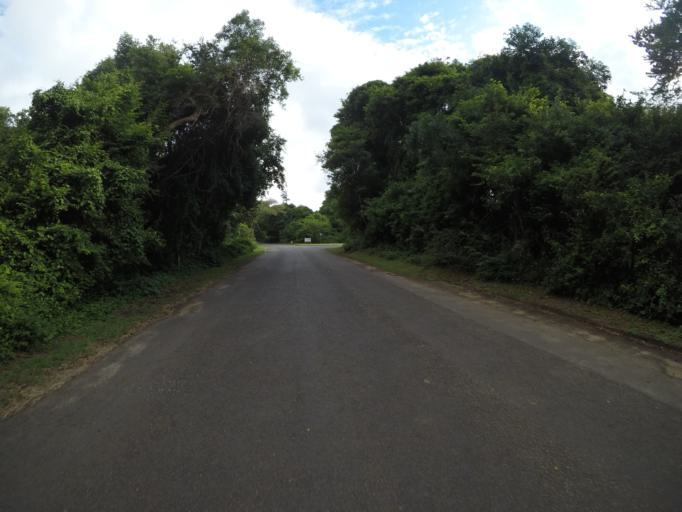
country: ZA
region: KwaZulu-Natal
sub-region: uMkhanyakude District Municipality
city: Mtubatuba
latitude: -28.3868
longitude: 32.4098
